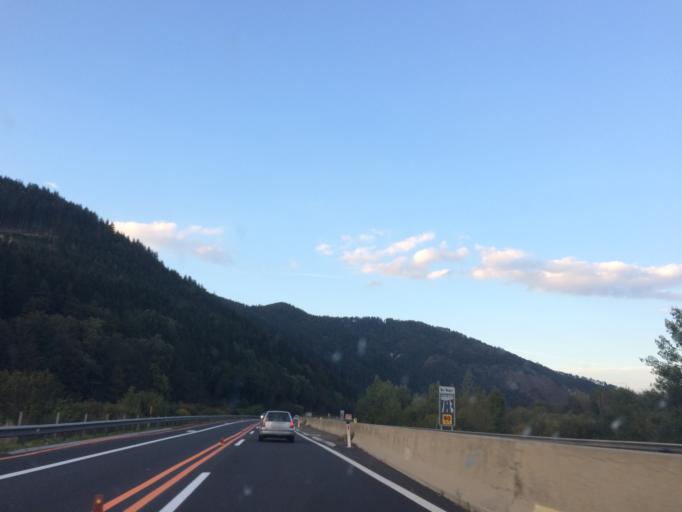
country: AT
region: Styria
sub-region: Politischer Bezirk Murtal
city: Feistritz bei Knittelfeld
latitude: 47.2680
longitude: 14.9113
